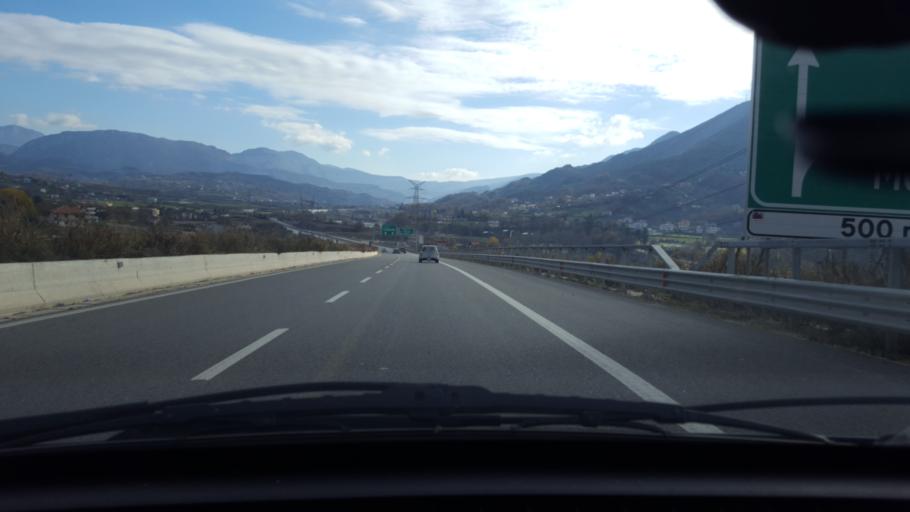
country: AL
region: Tirane
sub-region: Rrethi i Tiranes
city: Petrele
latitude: 41.2669
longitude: 19.8660
